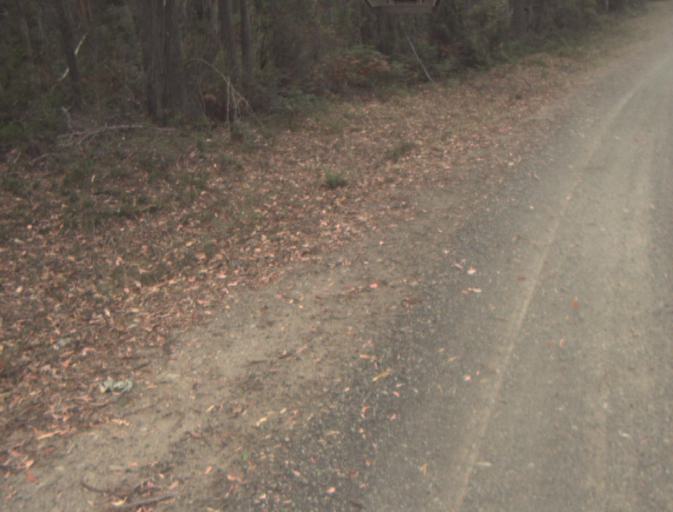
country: AU
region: Tasmania
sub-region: Dorset
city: Scottsdale
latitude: -41.4099
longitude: 147.5167
